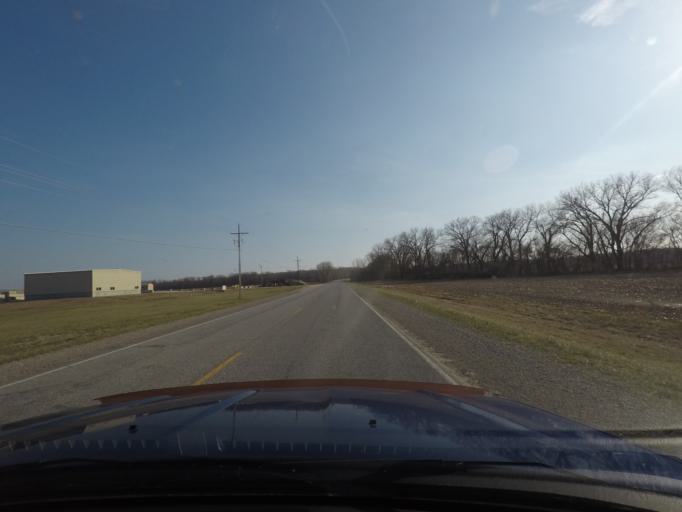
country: US
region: Kansas
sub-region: Douglas County
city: Lawrence
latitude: 39.0571
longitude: -95.3835
